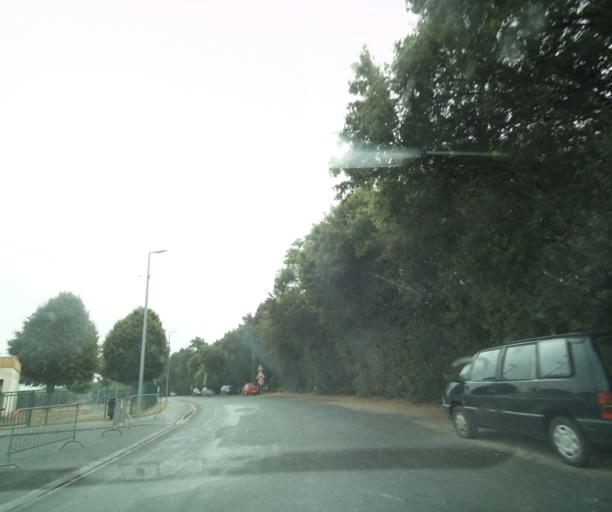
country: FR
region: Poitou-Charentes
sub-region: Departement de la Charente-Maritime
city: Tonnay-Charente
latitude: 45.9449
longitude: -0.9102
